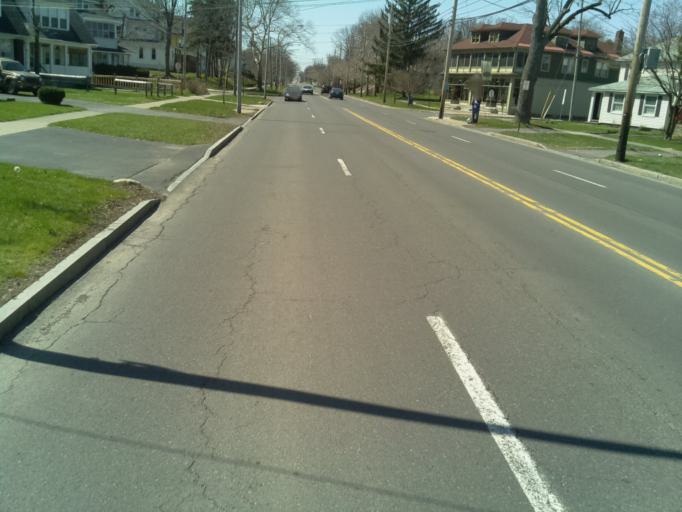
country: US
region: New York
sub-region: Onondaga County
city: Lyncourt
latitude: 43.0671
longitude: -76.1181
